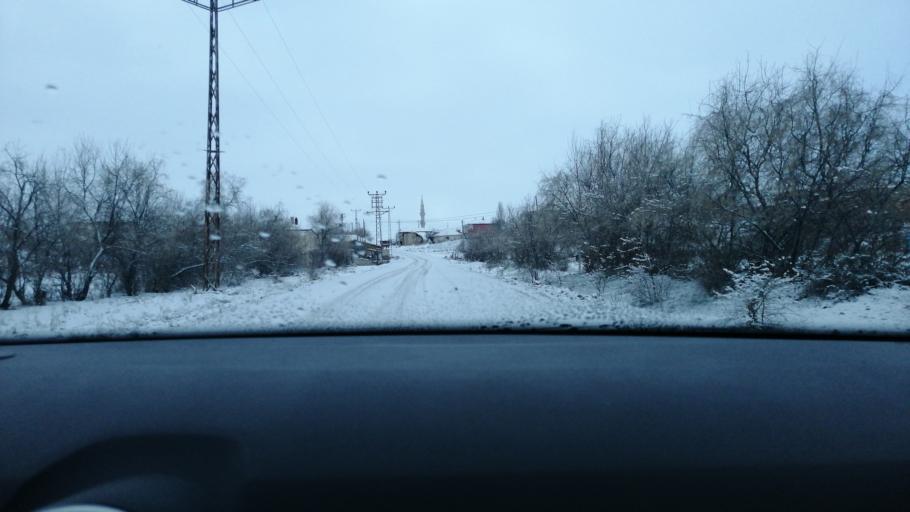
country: TR
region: Aksaray
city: Agacoren
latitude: 38.9366
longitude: 33.9484
